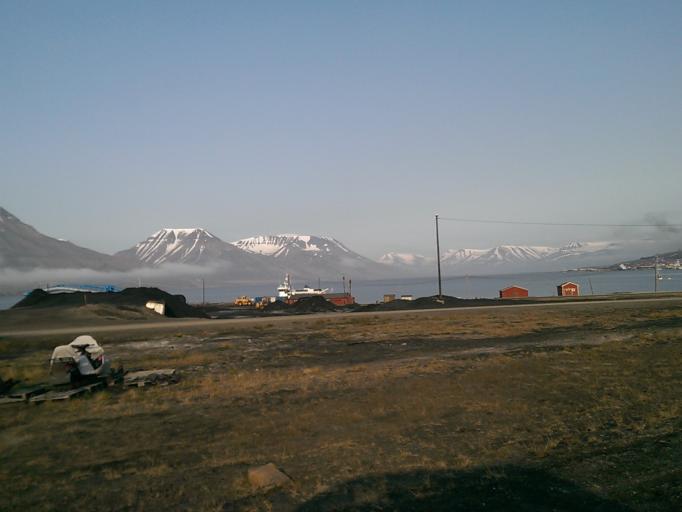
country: SJ
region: Svalbard
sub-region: Spitsbergen
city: Longyearbyen
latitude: 78.2436
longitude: 15.5307
